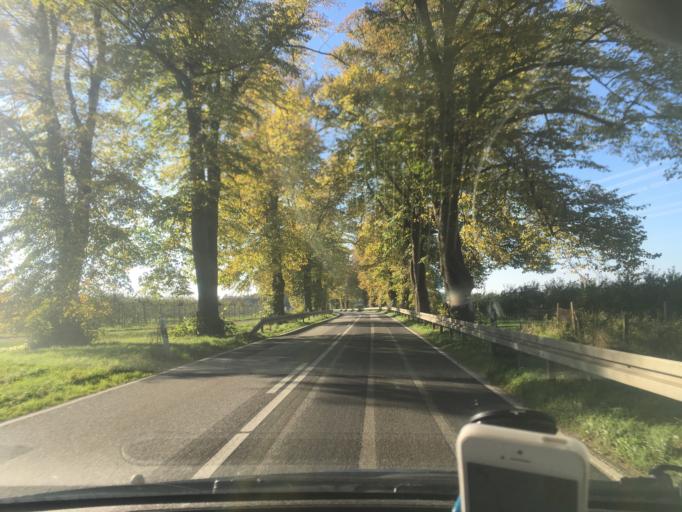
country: DE
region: Mecklenburg-Vorpommern
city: Wittenburg
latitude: 53.5192
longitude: 11.0345
